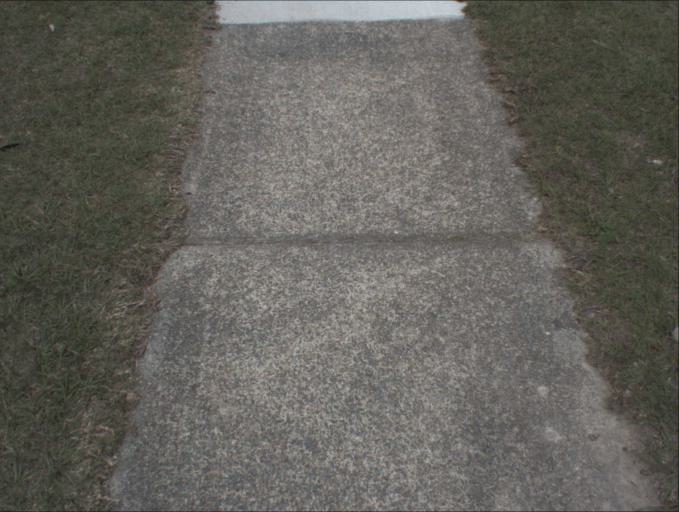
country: AU
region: Queensland
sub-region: Logan
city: Logan Reserve
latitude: -27.6860
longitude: 153.0881
